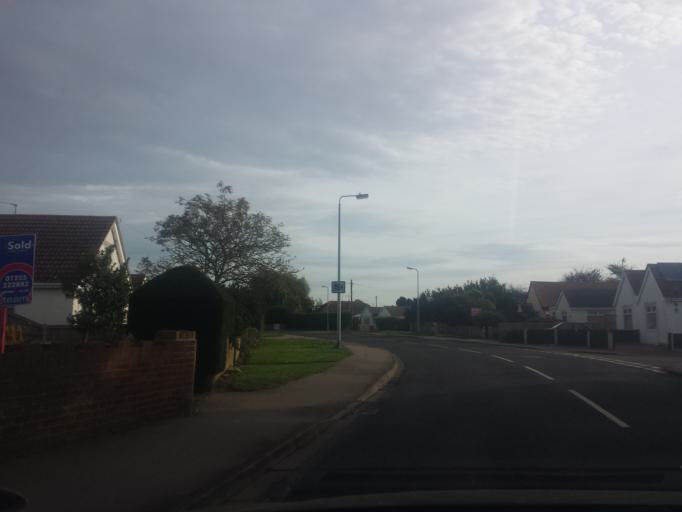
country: GB
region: England
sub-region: Essex
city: Clacton-on-Sea
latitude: 51.8104
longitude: 1.1694
